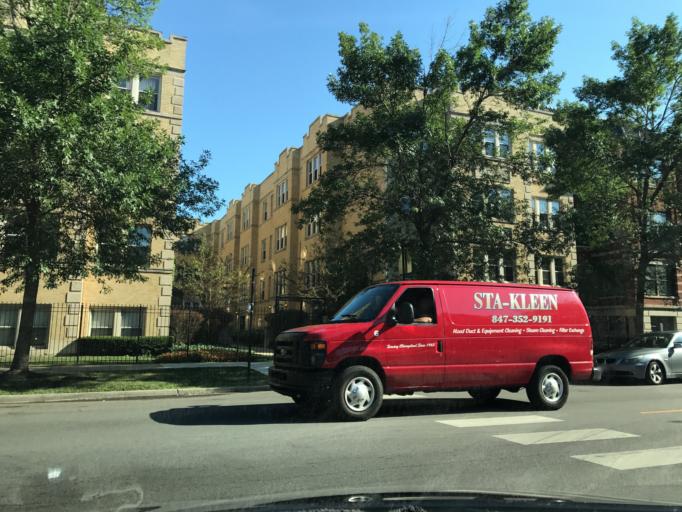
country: US
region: Illinois
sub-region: Cook County
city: Chicago
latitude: 41.8022
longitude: -87.5982
